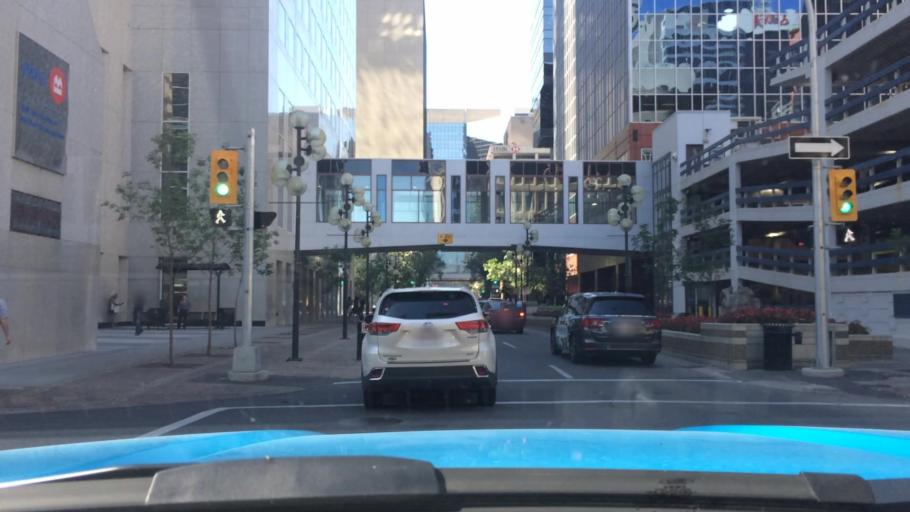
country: CA
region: Alberta
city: Calgary
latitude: 51.0477
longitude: -114.0702
